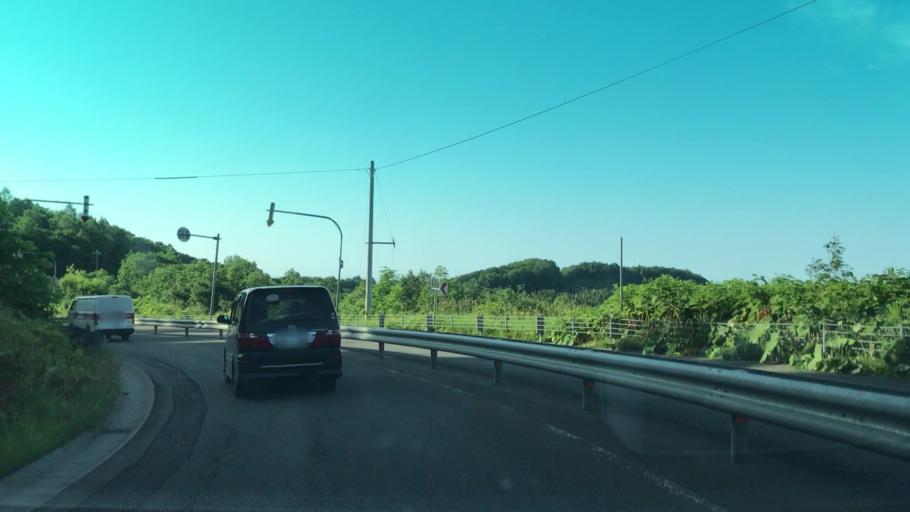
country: JP
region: Hokkaido
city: Otaru
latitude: 43.1398
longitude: 141.0148
